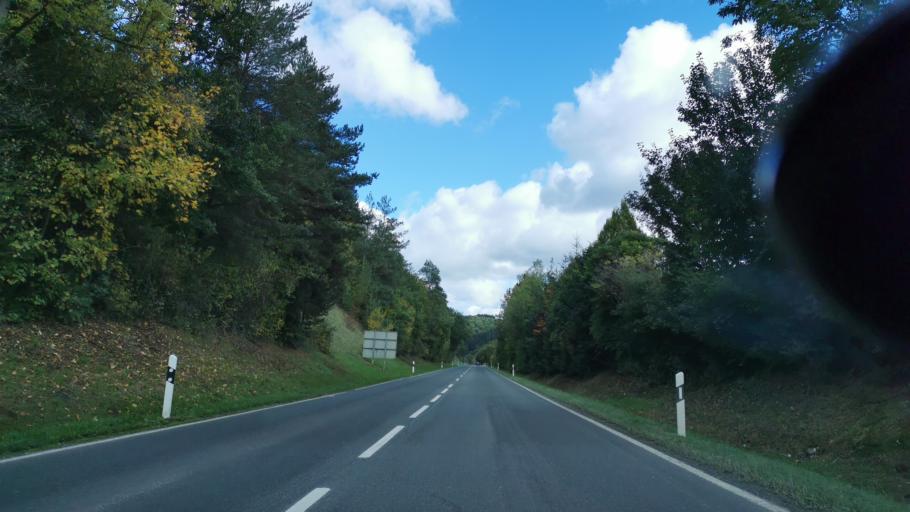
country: DE
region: Rheinland-Pfalz
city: Nohn
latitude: 50.3386
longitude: 6.7696
